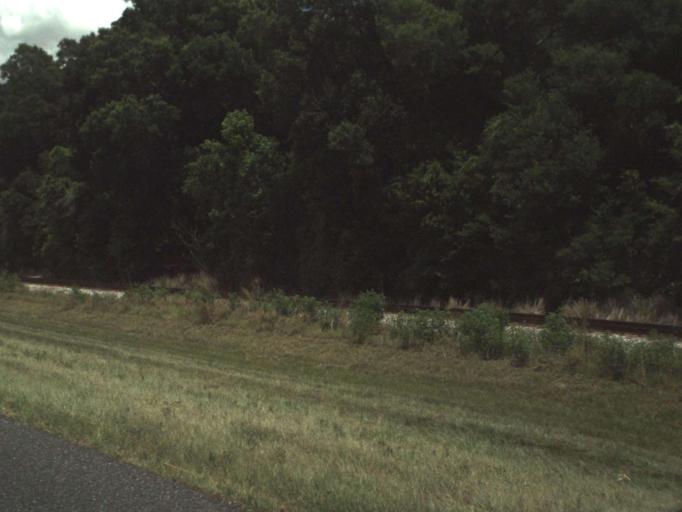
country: US
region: Florida
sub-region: Sumter County
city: The Villages
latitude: 28.9590
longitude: -82.0402
